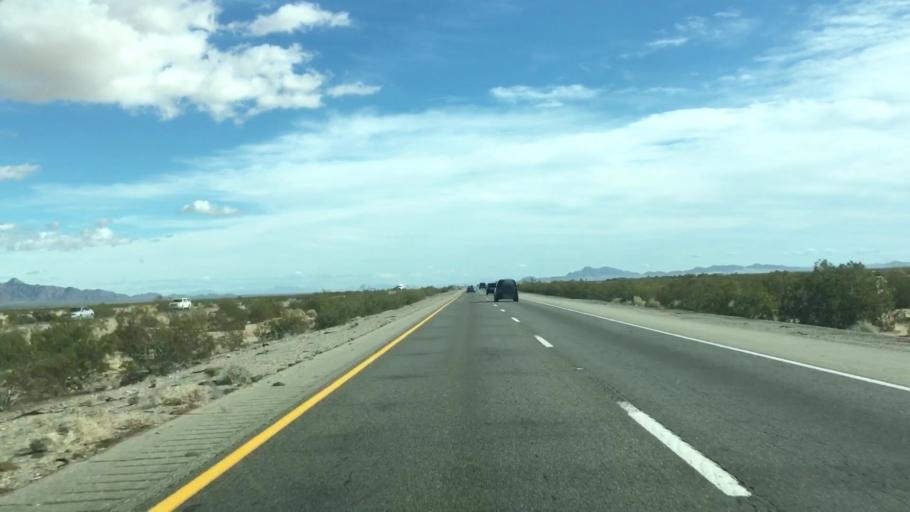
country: US
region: California
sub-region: Riverside County
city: Mesa Verde
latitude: 33.6231
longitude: -115.0451
